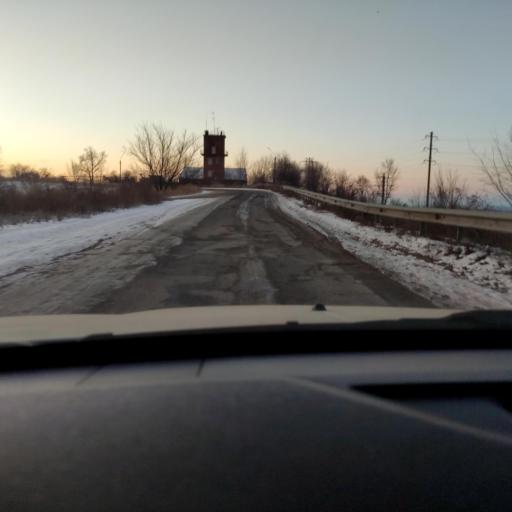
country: RU
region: Samara
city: Smyshlyayevka
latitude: 53.2419
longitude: 50.4798
